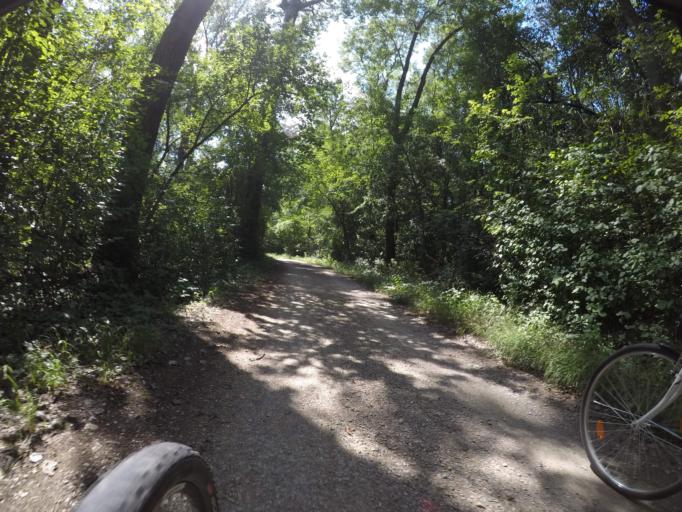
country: AT
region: Lower Austria
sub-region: Politischer Bezirk Ganserndorf
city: Gross-Enzersdorf
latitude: 48.1888
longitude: 16.5366
